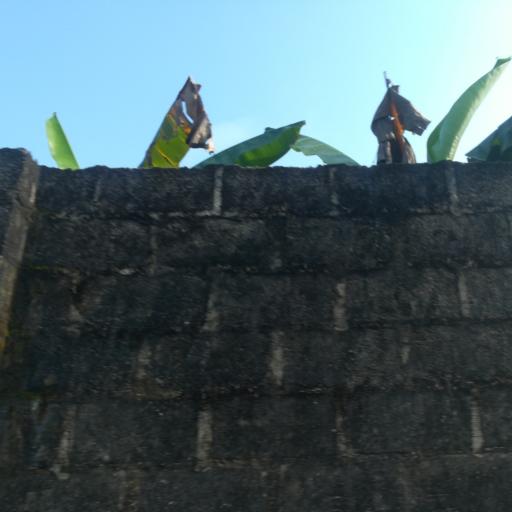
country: NG
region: Rivers
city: Port Harcourt
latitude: 4.8512
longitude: 6.9597
